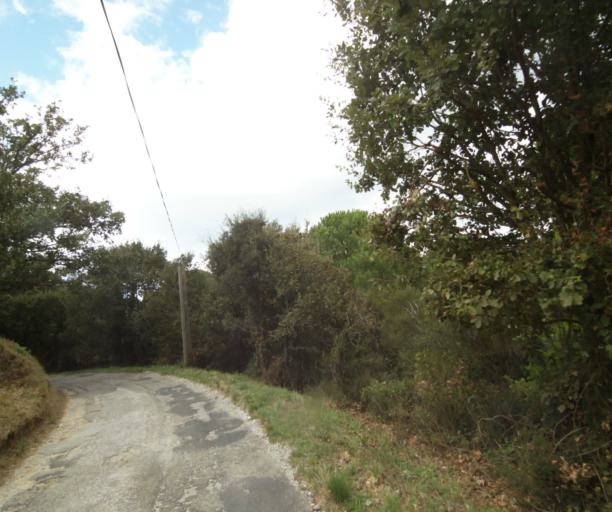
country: FR
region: Languedoc-Roussillon
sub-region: Departement des Pyrenees-Orientales
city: Argelers
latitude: 42.5403
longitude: 3.0131
